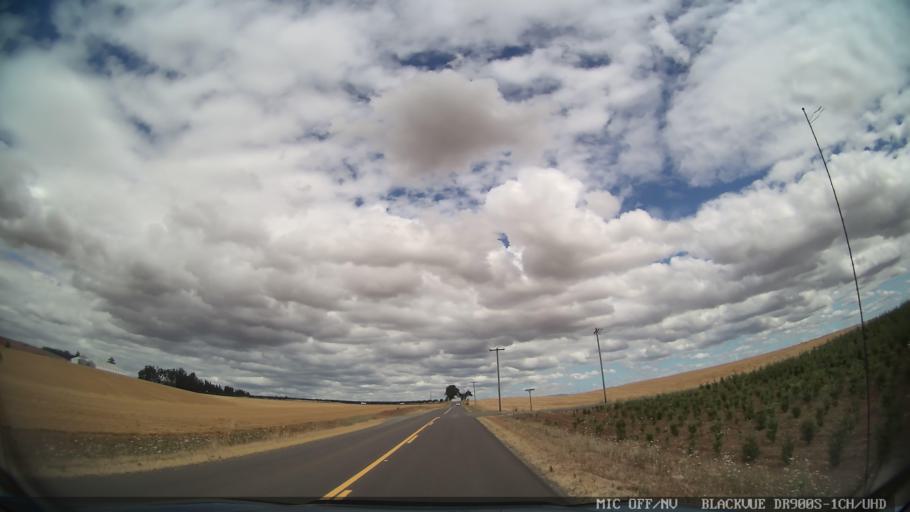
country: US
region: Oregon
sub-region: Marion County
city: Aumsville
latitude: 44.8654
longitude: -122.8434
